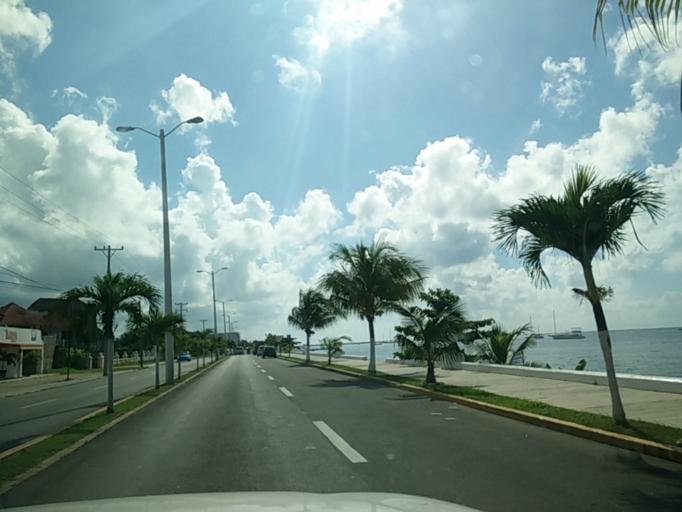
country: MX
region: Quintana Roo
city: San Miguel de Cozumel
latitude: 20.4914
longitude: -86.9663
